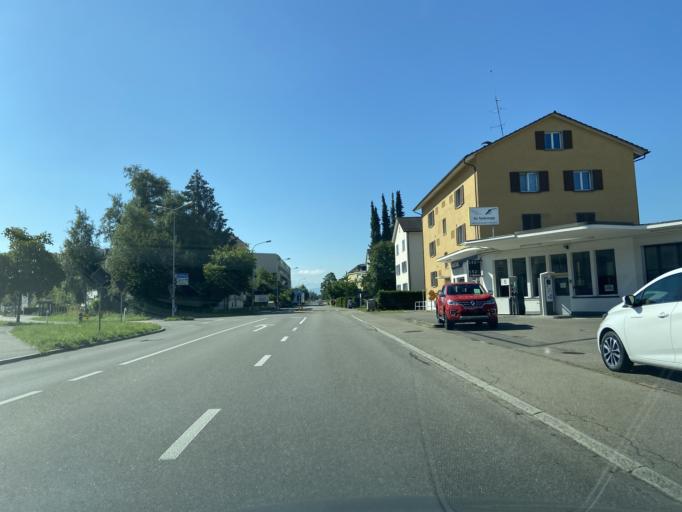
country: CH
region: Zurich
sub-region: Bezirk Uster
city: Uster / Gschwader
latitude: 47.3571
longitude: 8.7118
